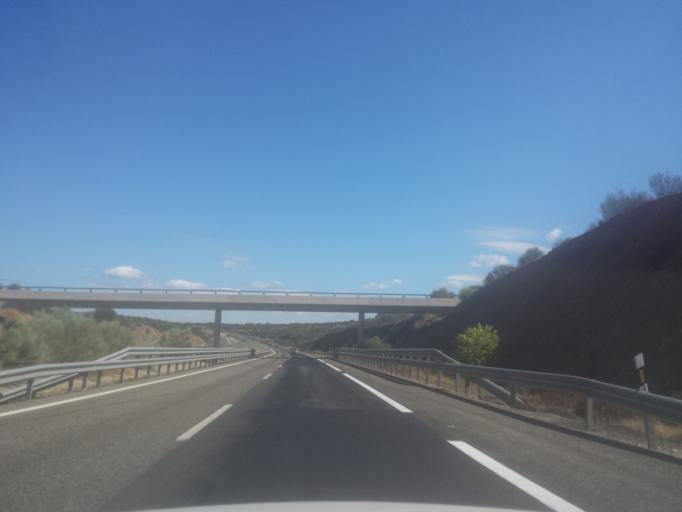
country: ES
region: Andalusia
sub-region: Provincia de Huelva
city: Santa Olalla del Cala
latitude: 37.8561
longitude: -6.2180
